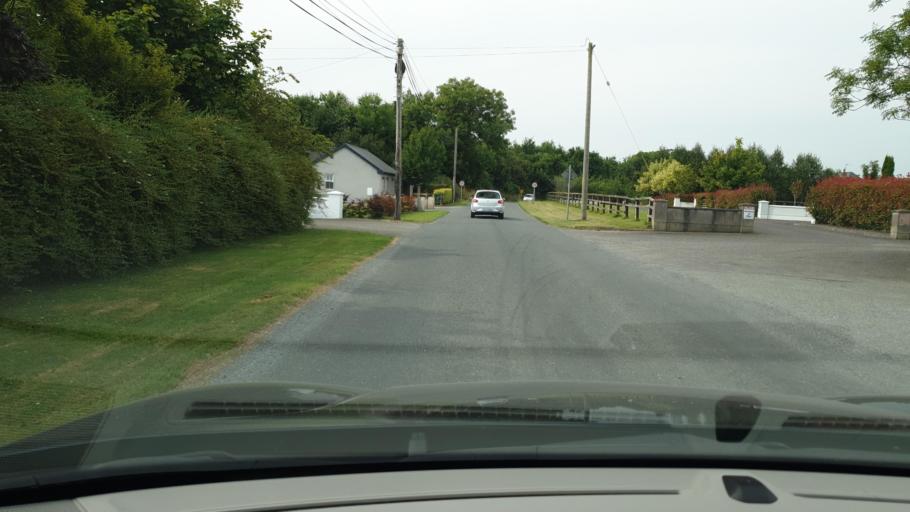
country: IE
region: Leinster
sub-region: An Mhi
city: Athboy
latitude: 53.6701
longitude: -6.9044
